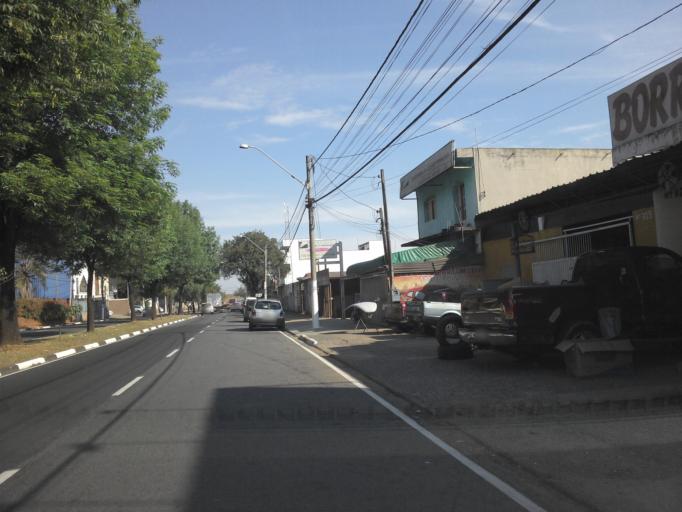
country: BR
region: Sao Paulo
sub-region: Hortolandia
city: Hortolandia
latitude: -22.9006
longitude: -47.2299
